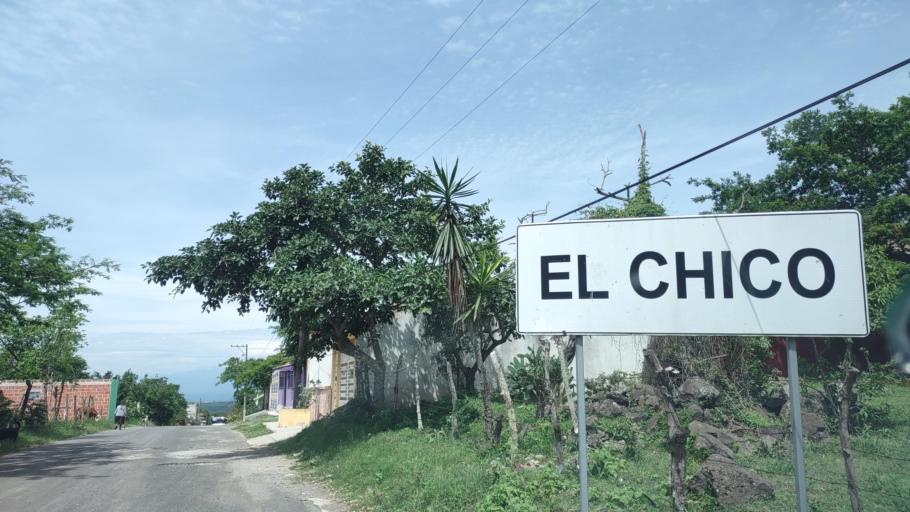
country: MX
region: Veracruz
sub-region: Emiliano Zapata
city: Dos Rios
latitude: 19.4693
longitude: -96.8305
